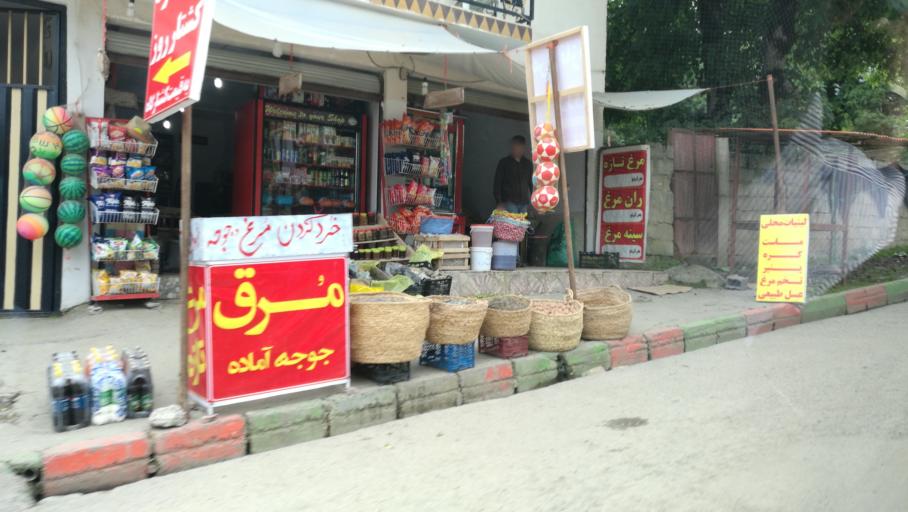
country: IR
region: Mazandaran
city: Ramsar
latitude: 36.8547
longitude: 50.4743
